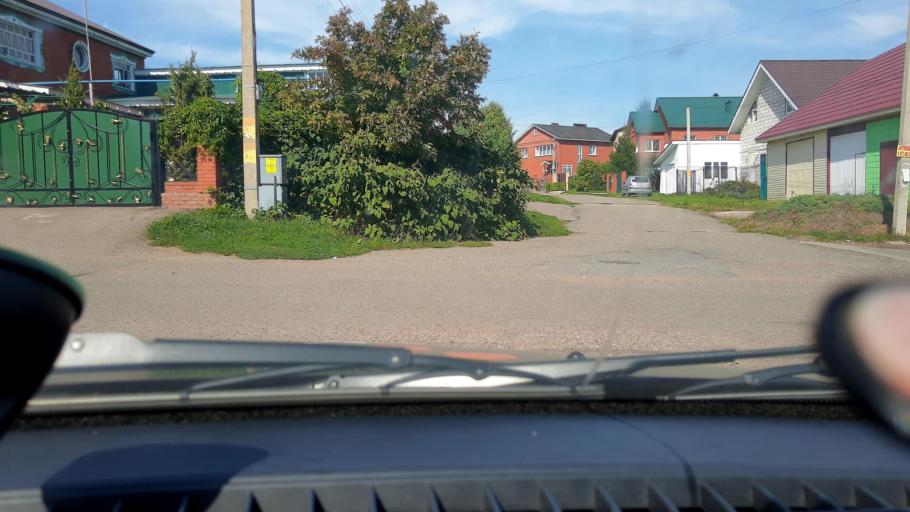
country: RU
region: Bashkortostan
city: Avdon
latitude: 54.6707
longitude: 55.7178
